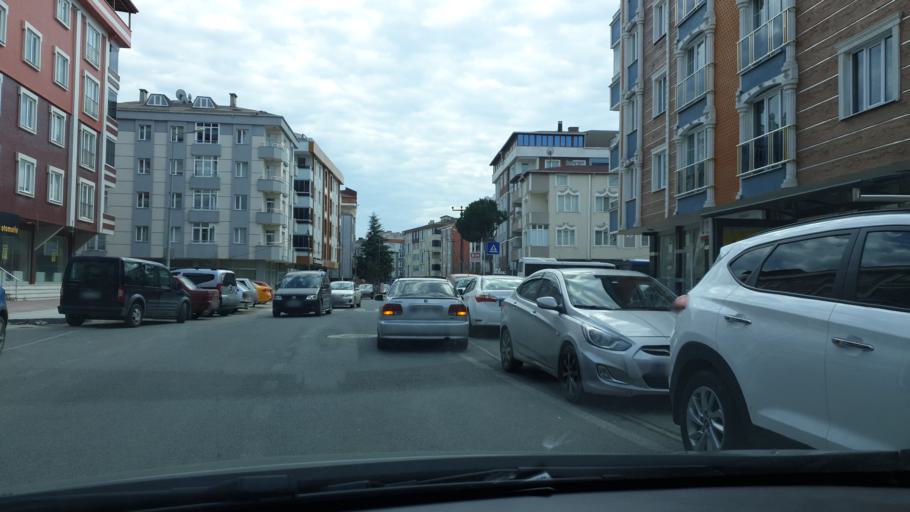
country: TR
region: Tekirdag
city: Cerkezkoey
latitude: 41.2865
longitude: 27.9931
